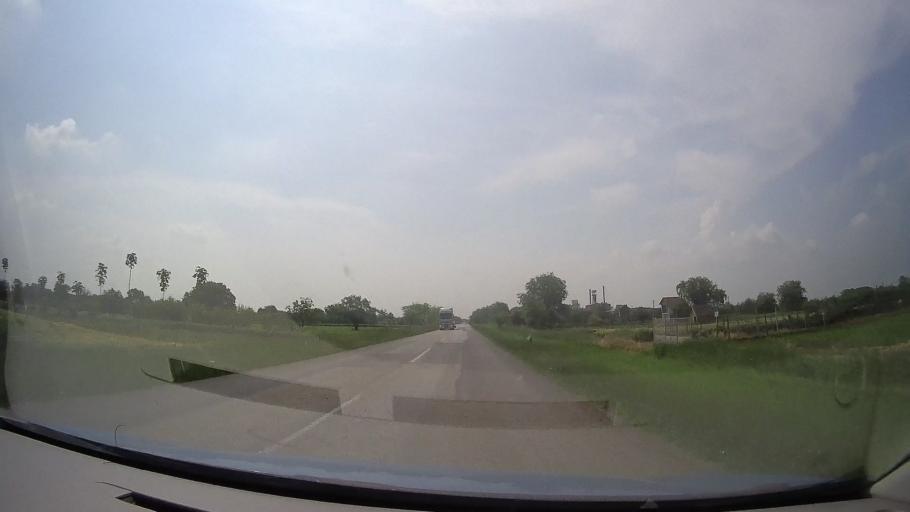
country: RS
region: Autonomna Pokrajina Vojvodina
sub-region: Juznobanatski Okrug
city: Kovacica
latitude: 45.0933
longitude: 20.6315
